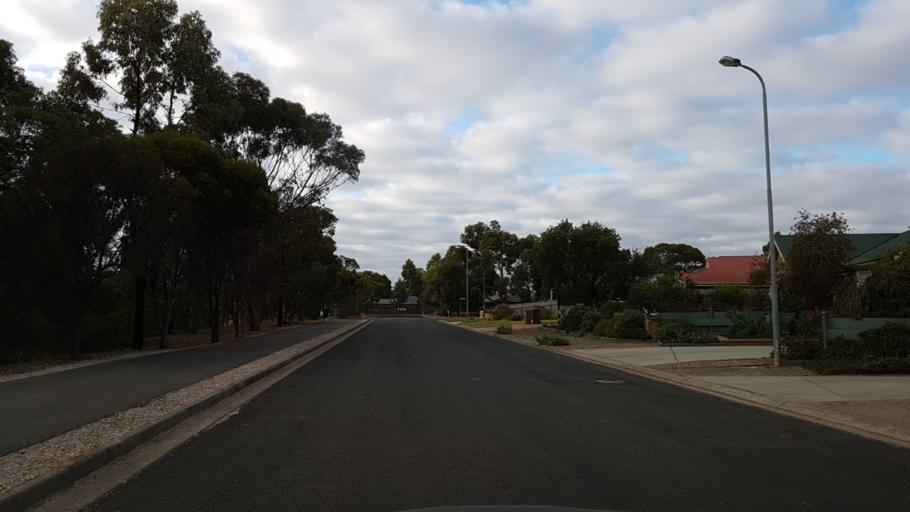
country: AU
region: South Australia
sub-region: Alexandrina
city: Strathalbyn
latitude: -35.2629
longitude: 138.9036
